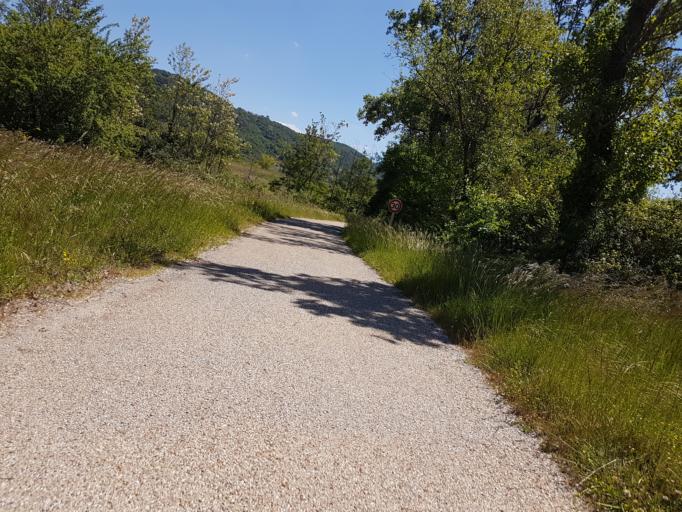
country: FR
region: Rhone-Alpes
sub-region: Departement de la Drome
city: Saint-Vallier
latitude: 45.1592
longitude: 4.8172
